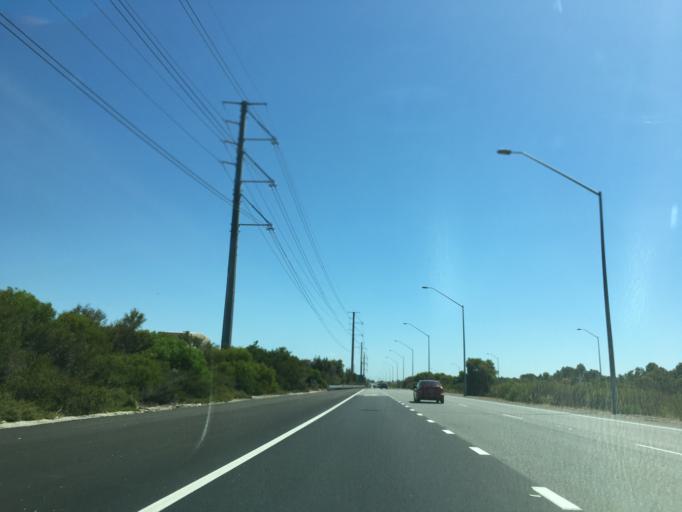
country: AU
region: Western Australia
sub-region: Canning
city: Willetton
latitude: -32.0598
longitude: 115.9017
